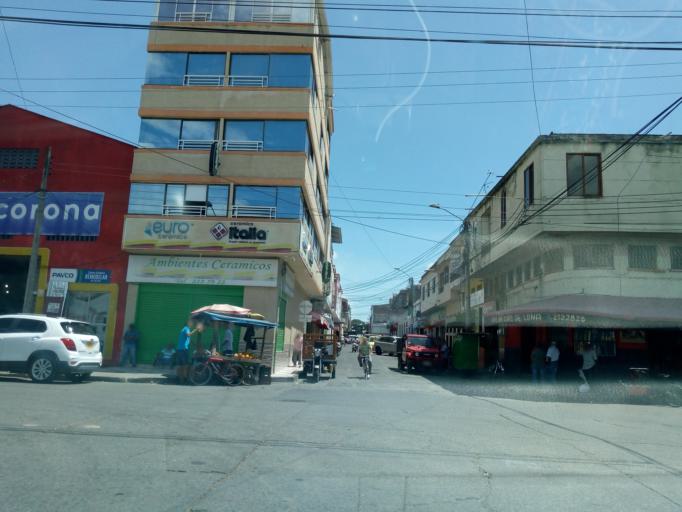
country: CO
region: Valle del Cauca
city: Cartago
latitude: 4.7470
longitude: -75.9147
